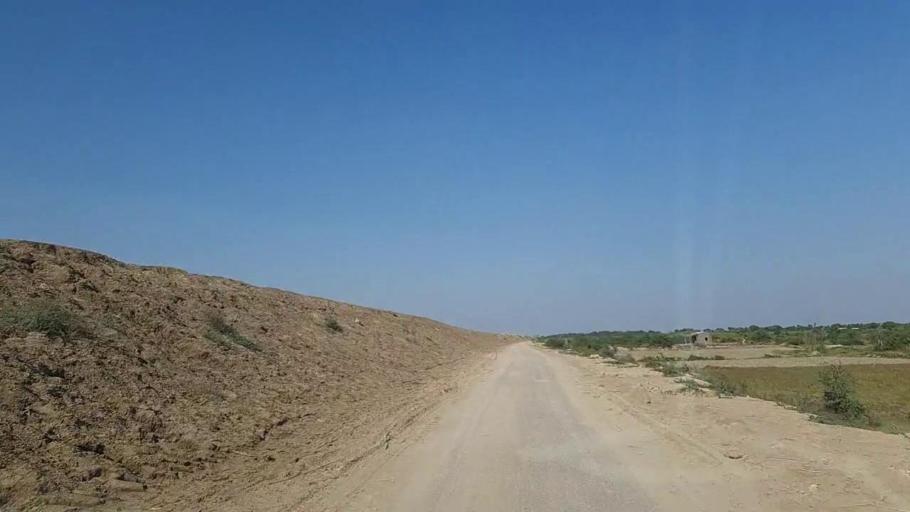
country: PK
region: Sindh
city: Chuhar Jamali
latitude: 24.5606
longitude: 68.0280
